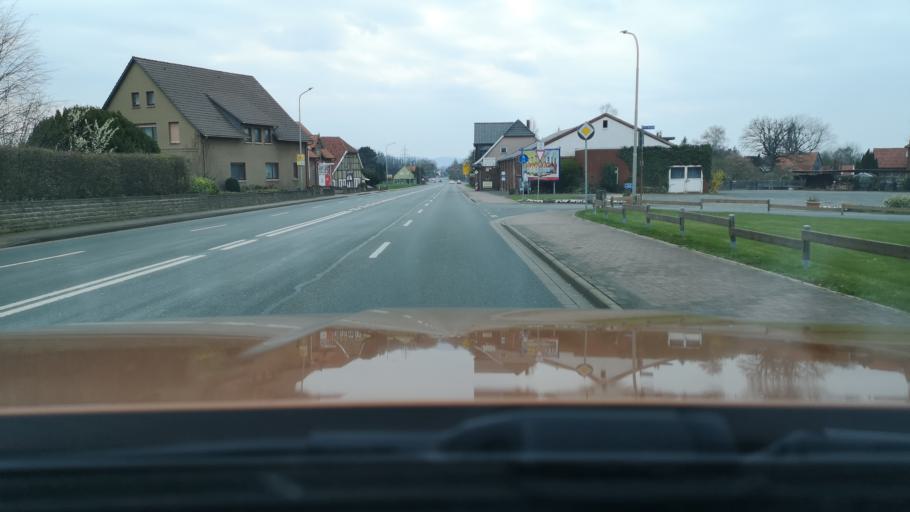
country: DE
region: Lower Saxony
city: Obernkirchen
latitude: 52.2825
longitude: 9.1270
